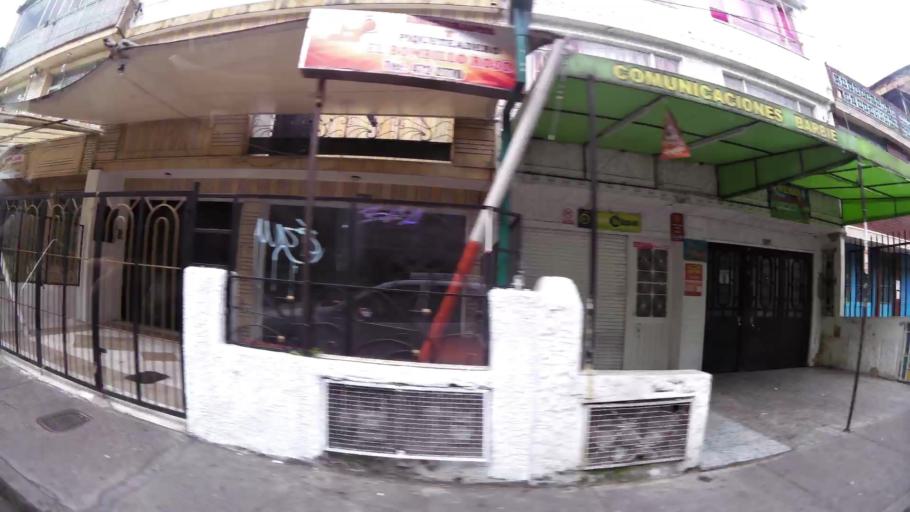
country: CO
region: Bogota D.C.
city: Bogota
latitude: 4.6143
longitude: -74.1095
